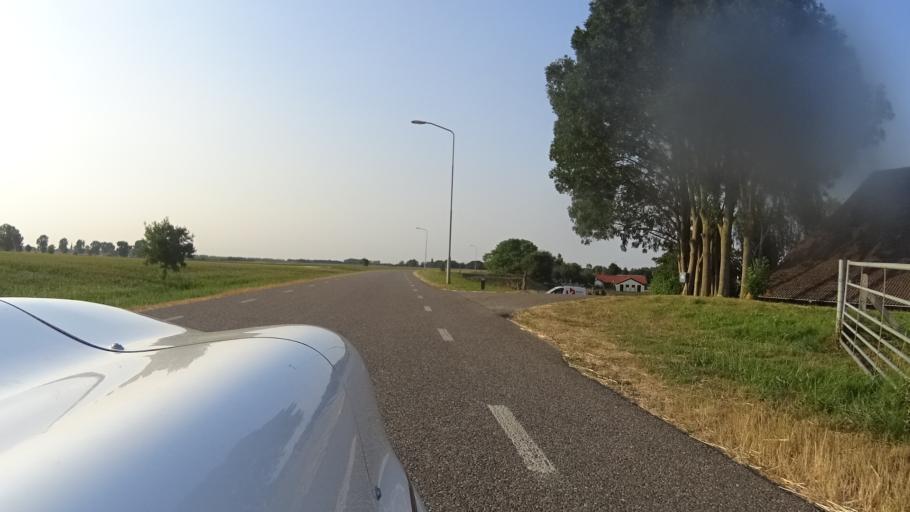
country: NL
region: Gelderland
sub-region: Gemeente Wijchen
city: Bergharen
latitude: 51.8047
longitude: 5.6565
